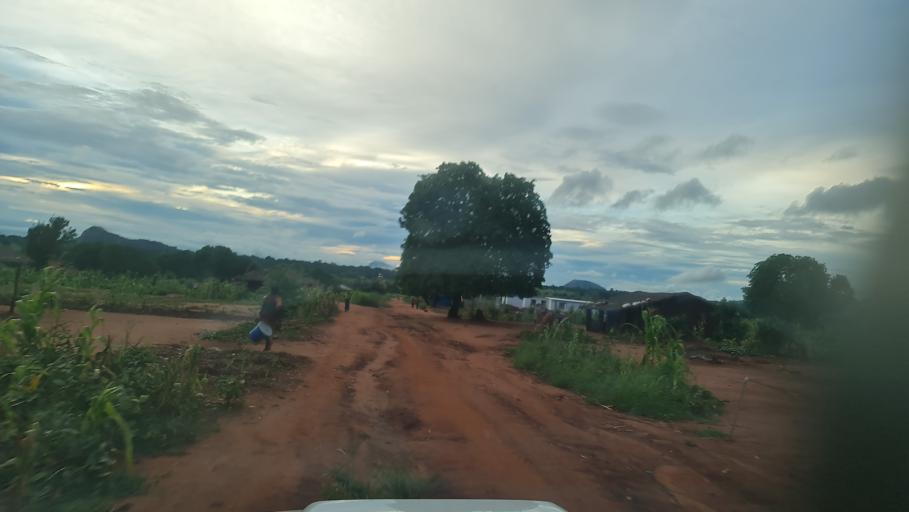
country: MZ
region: Nampula
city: Nacala
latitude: -14.7441
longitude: 39.9540
